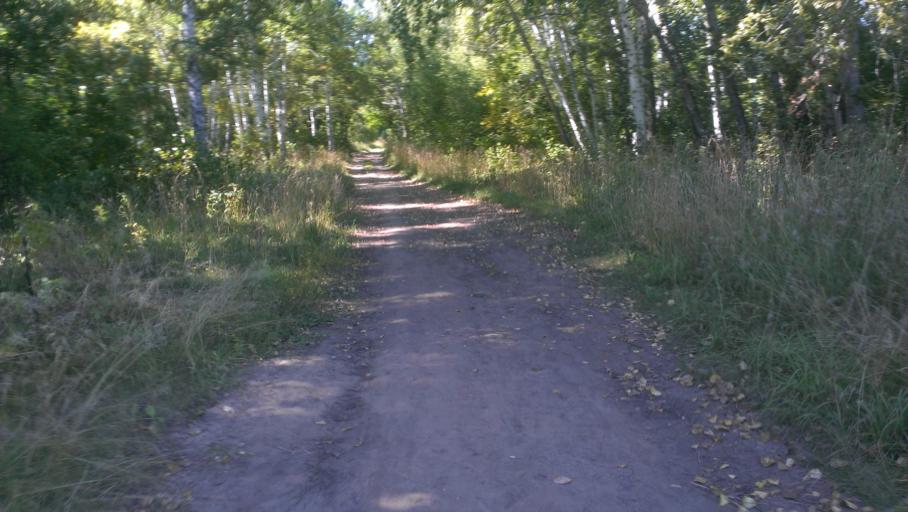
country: RU
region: Altai Krai
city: Nauchnyy Gorodok
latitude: 53.4232
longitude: 83.5121
